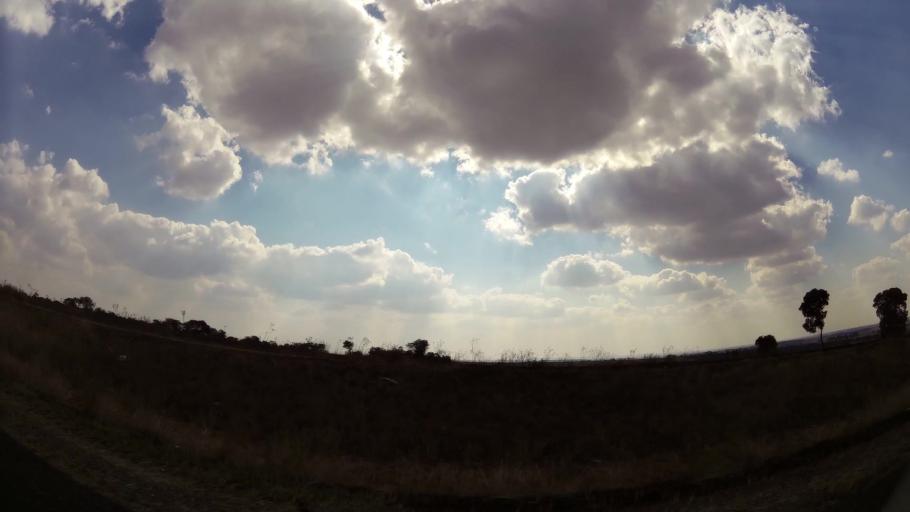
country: ZA
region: Mpumalanga
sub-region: Nkangala District Municipality
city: Delmas
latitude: -26.0929
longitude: 28.6739
